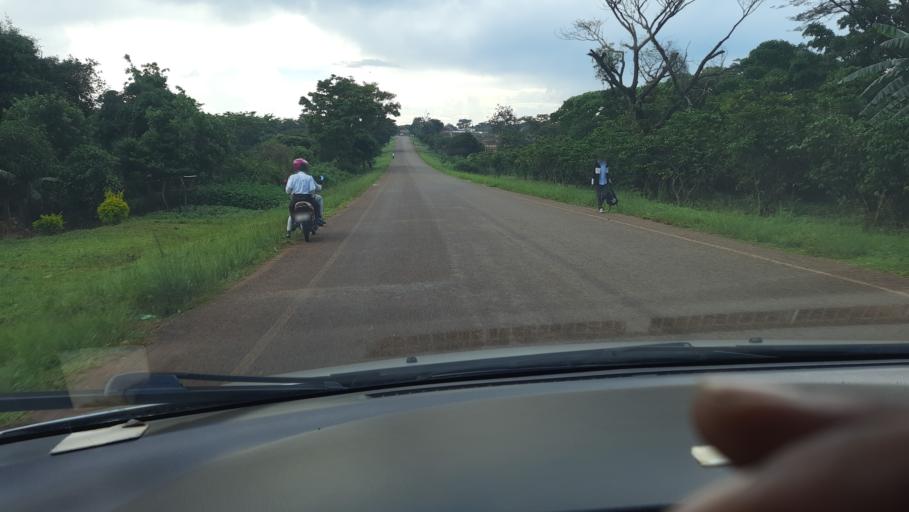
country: UG
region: Central Region
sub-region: Nakasongola District
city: Nakasongola
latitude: 1.3257
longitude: 32.4263
